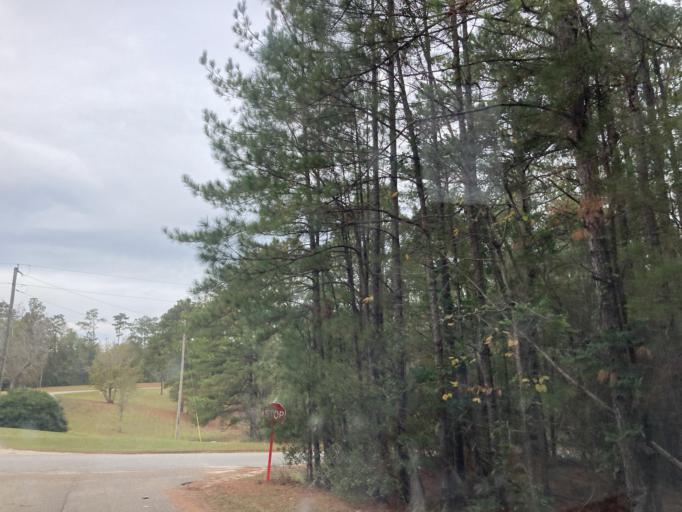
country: US
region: Mississippi
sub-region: Lamar County
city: Purvis
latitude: 31.1202
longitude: -89.4546
